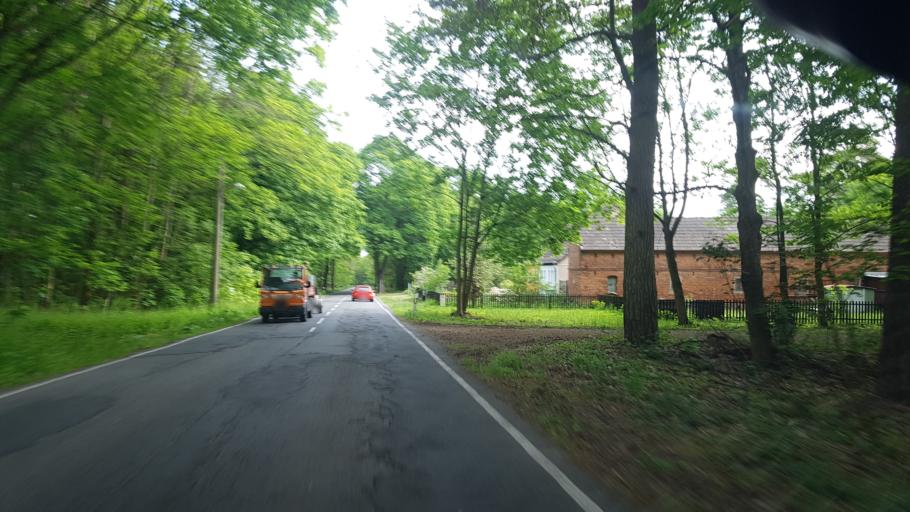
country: DE
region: Brandenburg
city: Baruth
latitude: 52.0136
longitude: 13.4705
